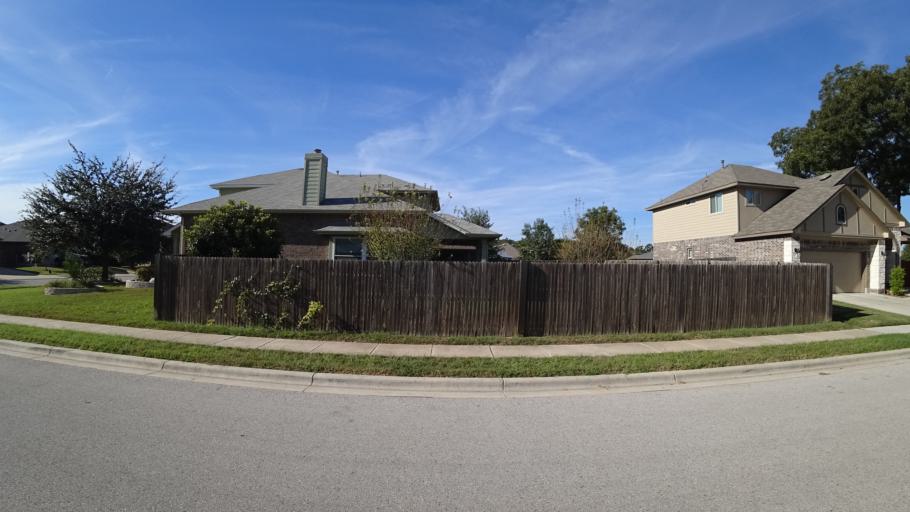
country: US
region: Texas
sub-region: Travis County
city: Austin
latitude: 30.2599
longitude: -97.6679
